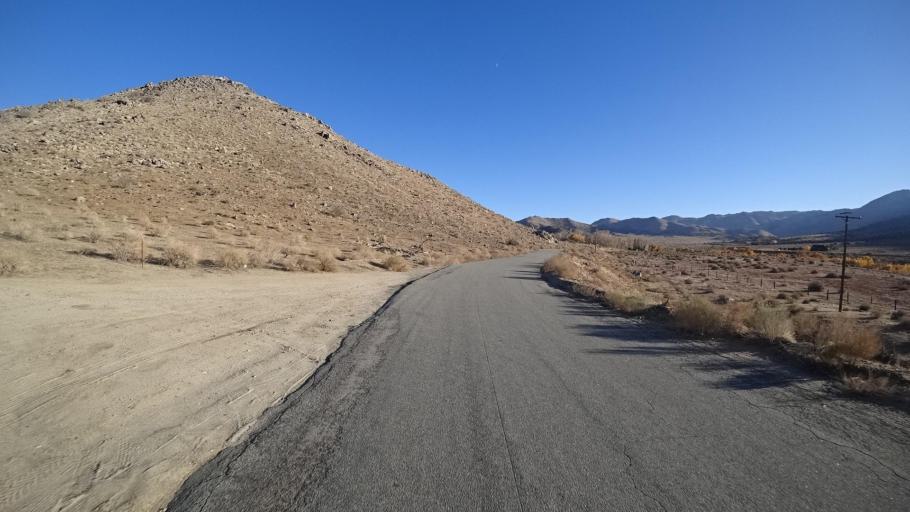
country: US
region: California
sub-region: Kern County
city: Weldon
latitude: 35.5688
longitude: -118.2485
